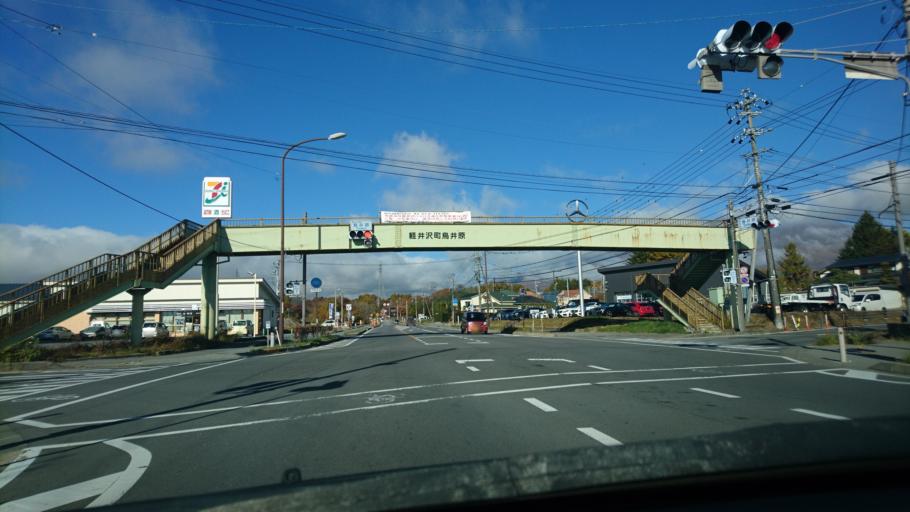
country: JP
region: Nagano
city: Komoro
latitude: 36.3381
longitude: 138.5882
